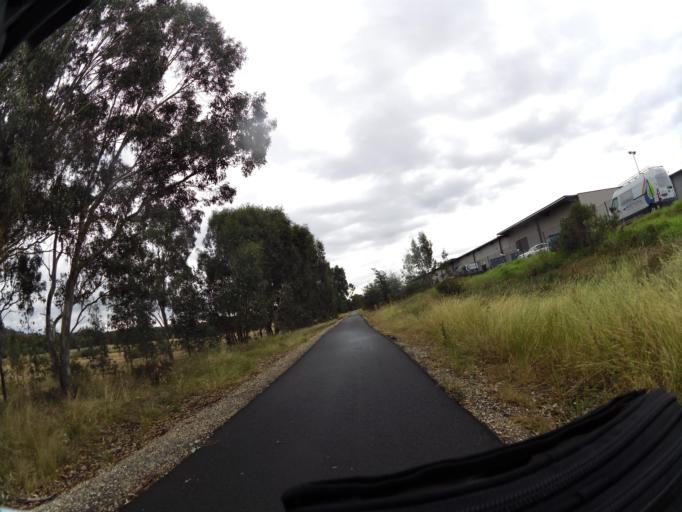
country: AU
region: Victoria
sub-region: Wodonga
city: Wodonga
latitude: -36.1393
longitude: 146.9091
